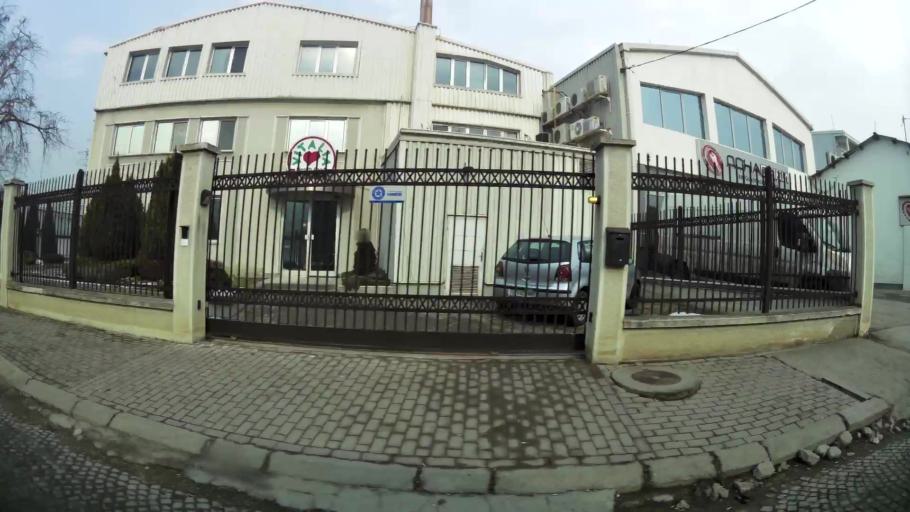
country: MK
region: Karpos
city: Skopje
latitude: 41.9942
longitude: 21.4540
